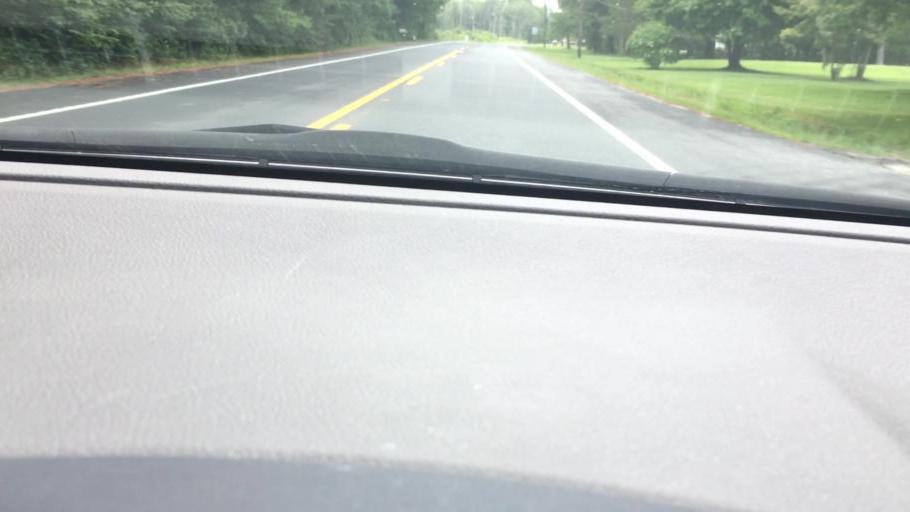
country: US
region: Maryland
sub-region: Worcester County
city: Pocomoke City
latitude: 38.0659
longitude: -75.5226
